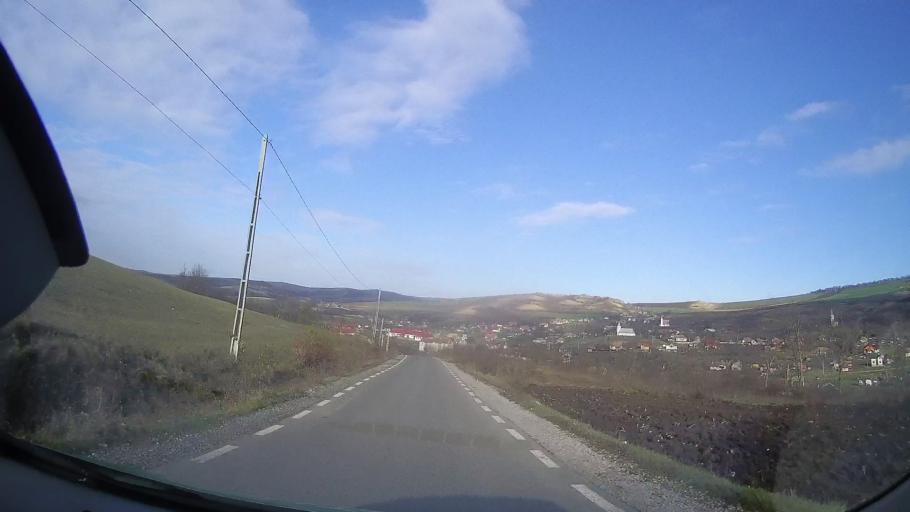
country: RO
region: Mures
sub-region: Comuna Sanger
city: Sanger
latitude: 46.5534
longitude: 24.1426
